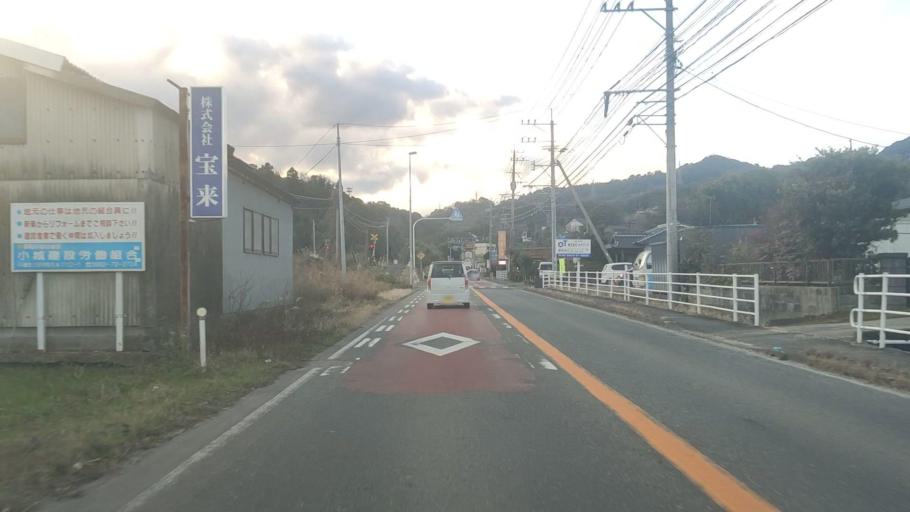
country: JP
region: Saga Prefecture
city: Saga-shi
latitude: 33.2909
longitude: 130.1738
